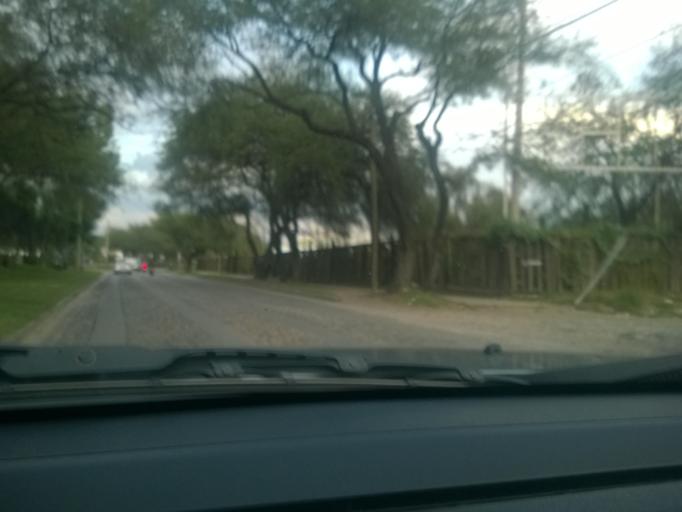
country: MX
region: Guanajuato
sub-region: Leon
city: Medina
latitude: 21.1129
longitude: -101.6218
